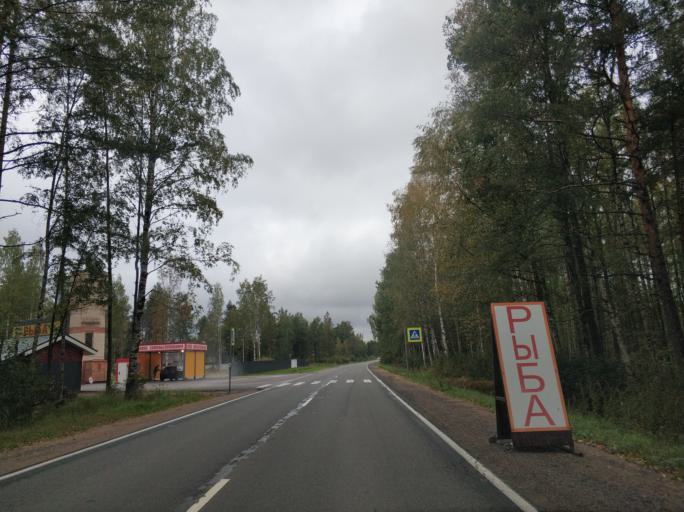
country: RU
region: Leningrad
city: Borisova Griva
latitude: 60.0917
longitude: 30.8562
